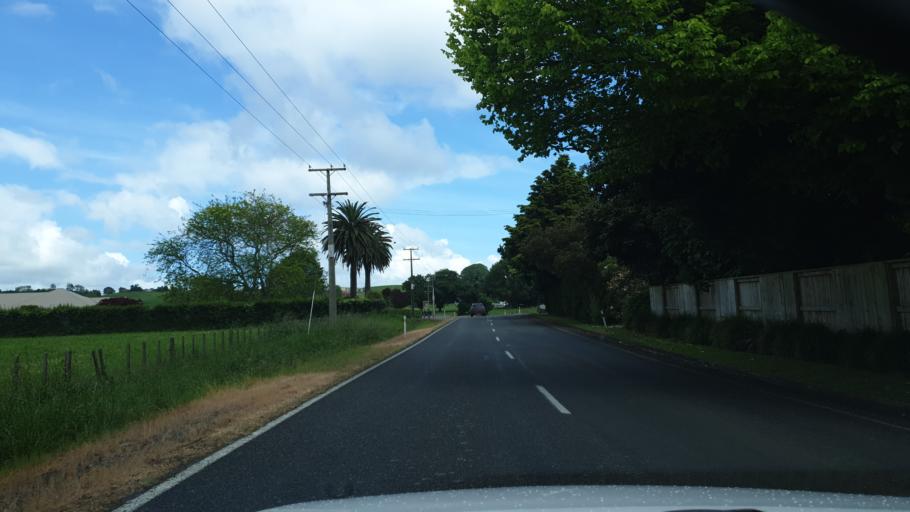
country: NZ
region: Waikato
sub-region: Matamata-Piako District
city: Matamata
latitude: -37.8782
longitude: 175.7090
